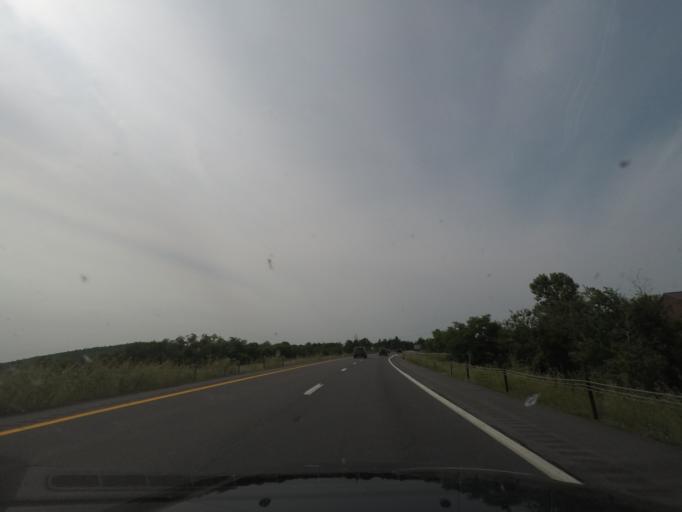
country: US
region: New York
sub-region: Essex County
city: Keeseville
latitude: 44.4937
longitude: -73.4979
